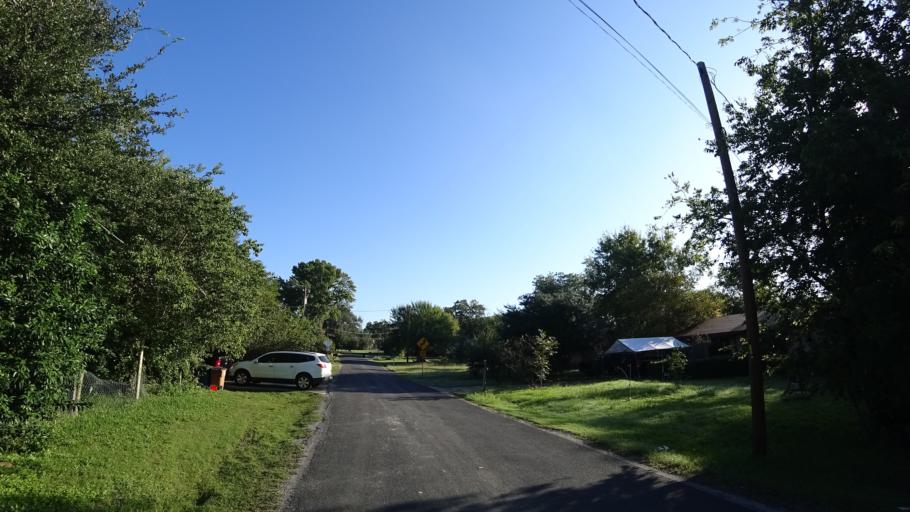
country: US
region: Texas
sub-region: Travis County
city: Wells Branch
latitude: 30.3548
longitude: -97.6932
